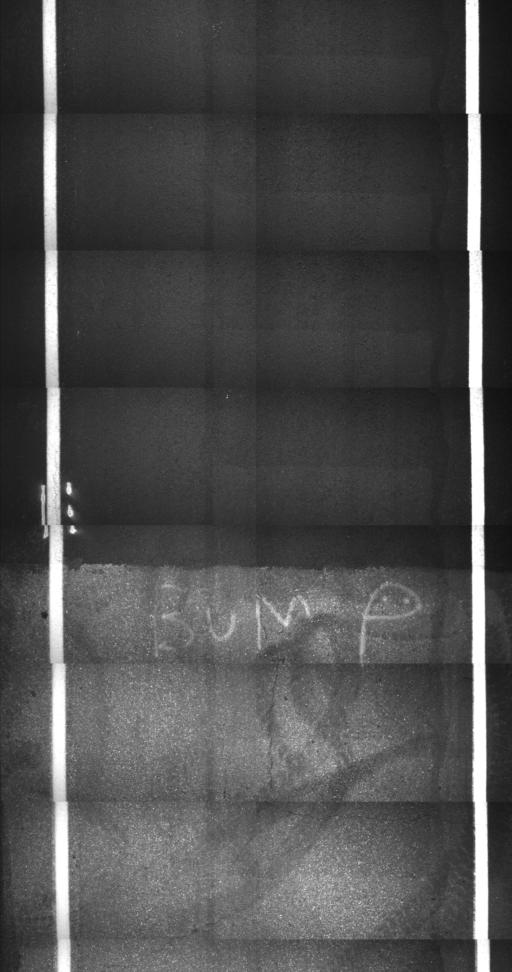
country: US
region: Vermont
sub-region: Caledonia County
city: Lyndonville
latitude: 44.6436
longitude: -71.8938
